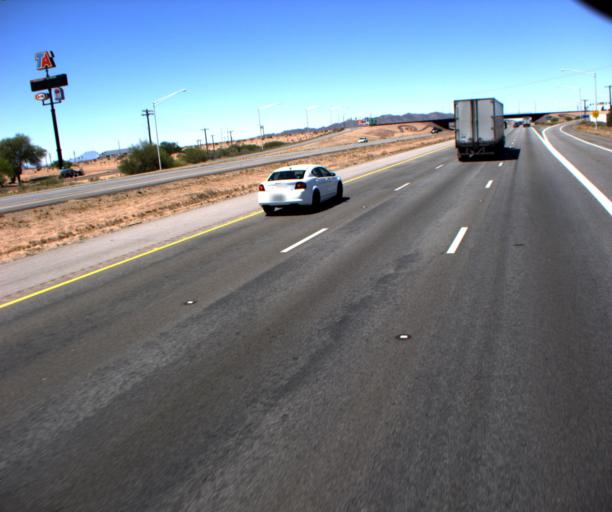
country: US
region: Arizona
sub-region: Pinal County
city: Arizona City
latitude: 32.7748
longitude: -111.6151
